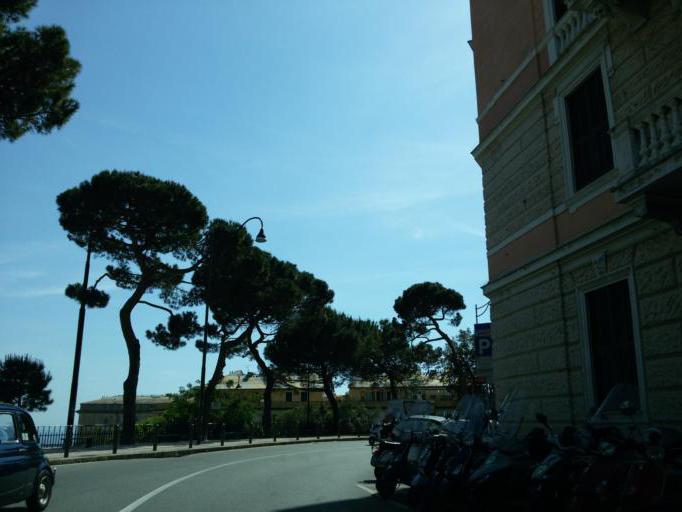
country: IT
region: Liguria
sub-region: Provincia di Genova
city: Genoa
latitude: 44.4186
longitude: 8.9279
